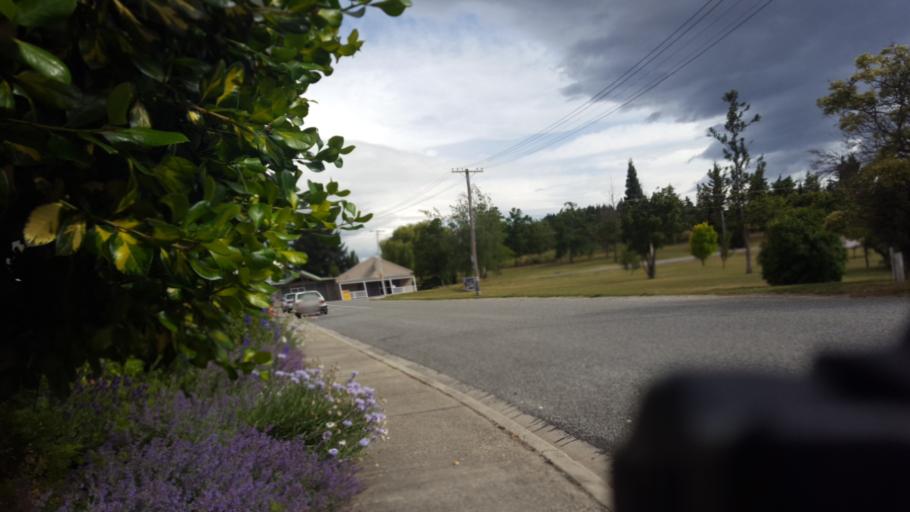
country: NZ
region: Otago
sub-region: Queenstown-Lakes District
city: Wanaka
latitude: -45.2487
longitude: 169.4007
